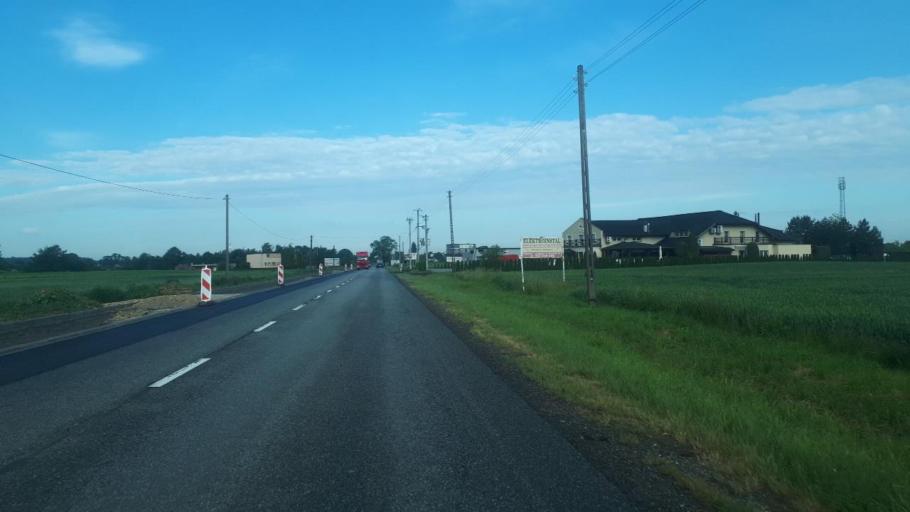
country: PL
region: Silesian Voivodeship
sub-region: Powiat pszczynski
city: Jankowice
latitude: 49.9710
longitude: 19.0028
